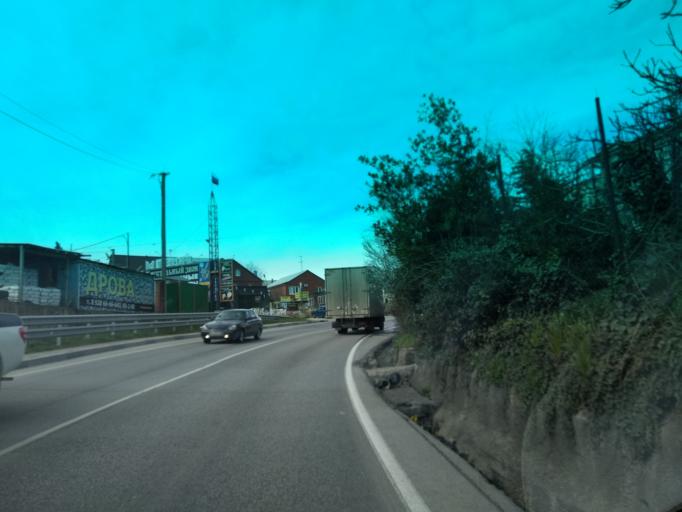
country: RU
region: Krasnodarskiy
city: Tuapse
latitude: 44.0936
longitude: 39.1142
